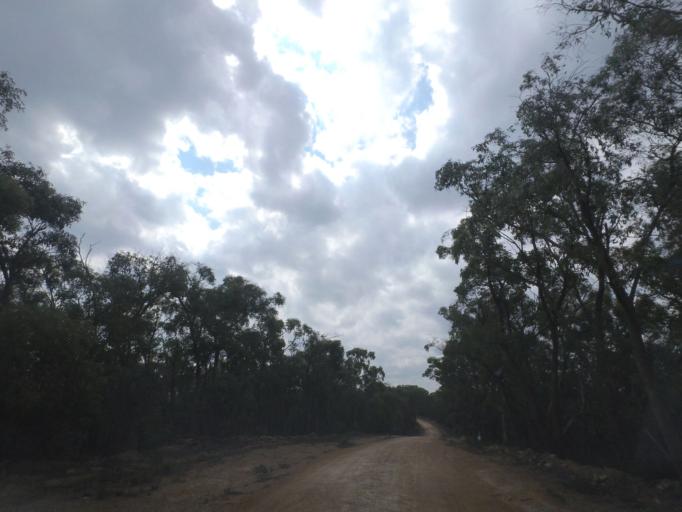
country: AU
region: Victoria
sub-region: Moorabool
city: Bacchus Marsh
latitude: -37.5475
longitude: 144.4253
